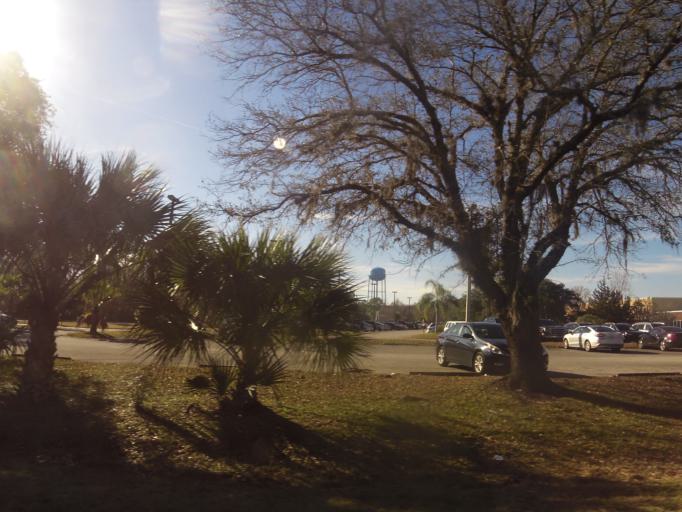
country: US
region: Florida
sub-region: Saint Johns County
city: Saint Augustine
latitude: 29.9194
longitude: -81.4032
